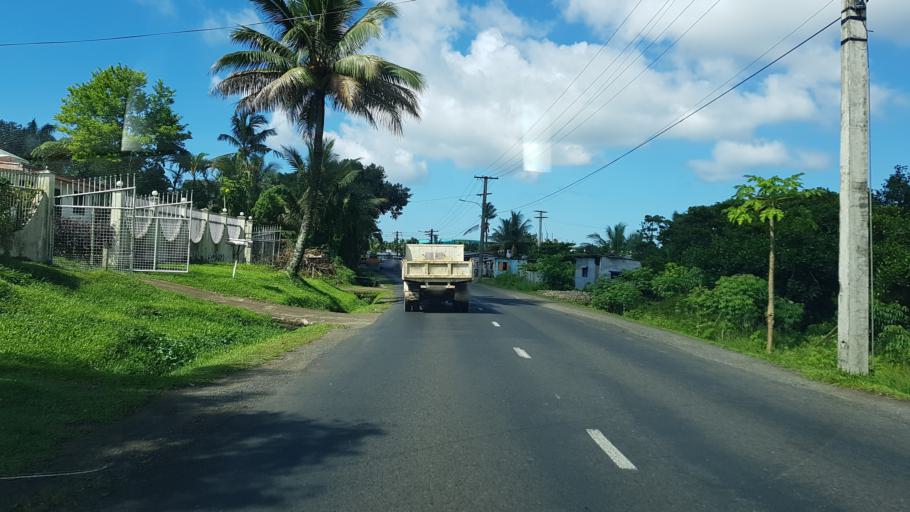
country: FJ
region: Central
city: Suva
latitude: -18.1423
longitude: 178.4554
